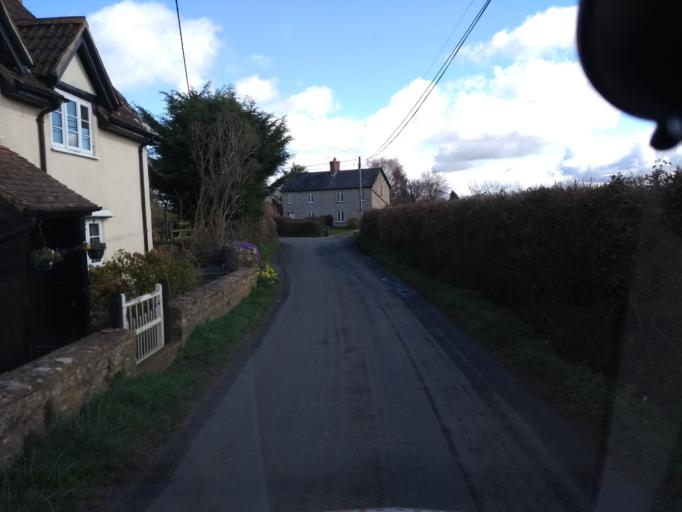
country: GB
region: England
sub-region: Somerset
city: Creech Saint Michael
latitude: 50.9671
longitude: -3.0143
